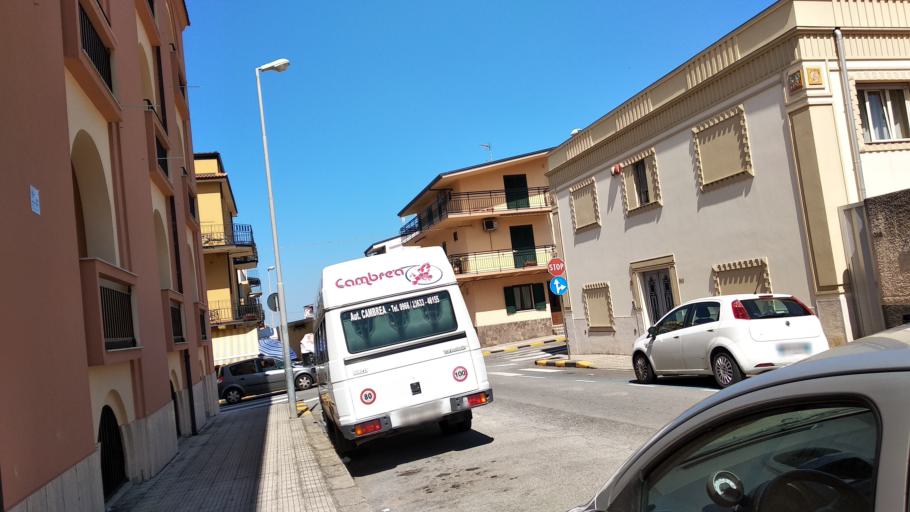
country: IT
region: Calabria
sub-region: Provincia di Reggio Calabria
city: Seminara
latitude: 38.3597
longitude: 15.8492
